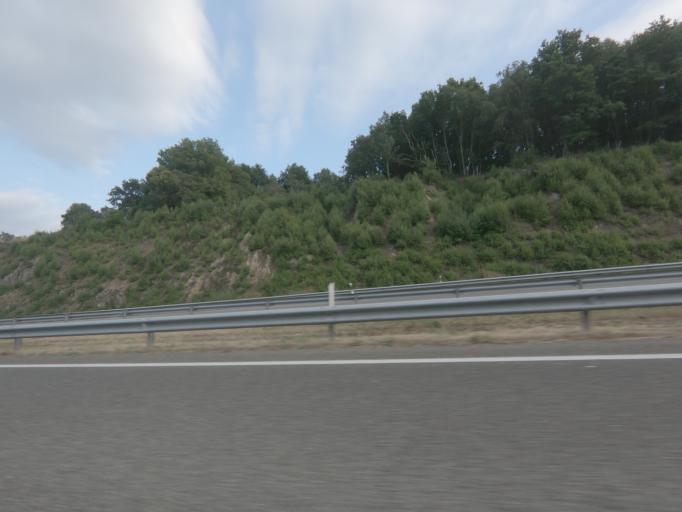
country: ES
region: Galicia
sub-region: Provincia de Ourense
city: Allariz
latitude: 42.2026
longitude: -7.7932
